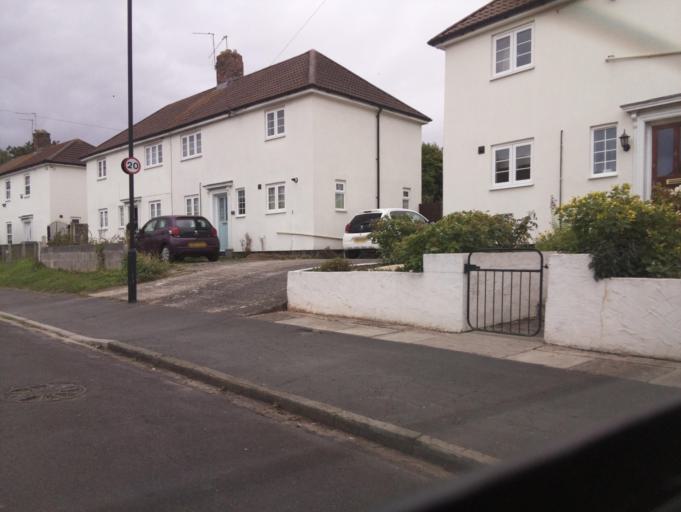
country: GB
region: England
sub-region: North Somerset
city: Easton-in-Gordano
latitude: 51.4921
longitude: -2.6509
